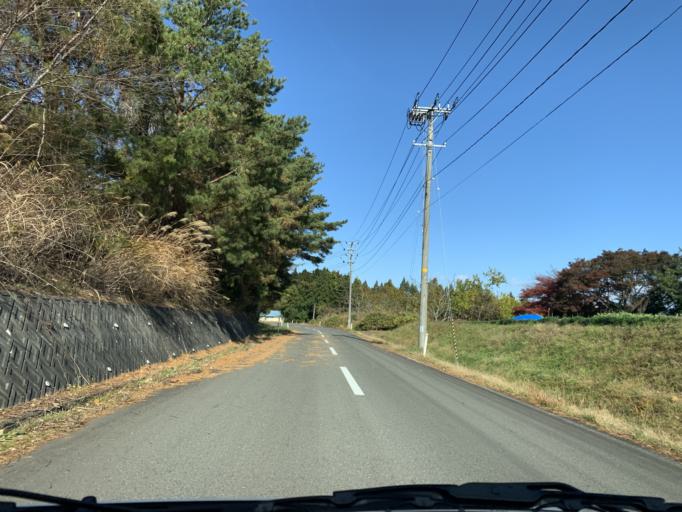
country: JP
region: Iwate
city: Mizusawa
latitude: 39.0600
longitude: 141.1122
